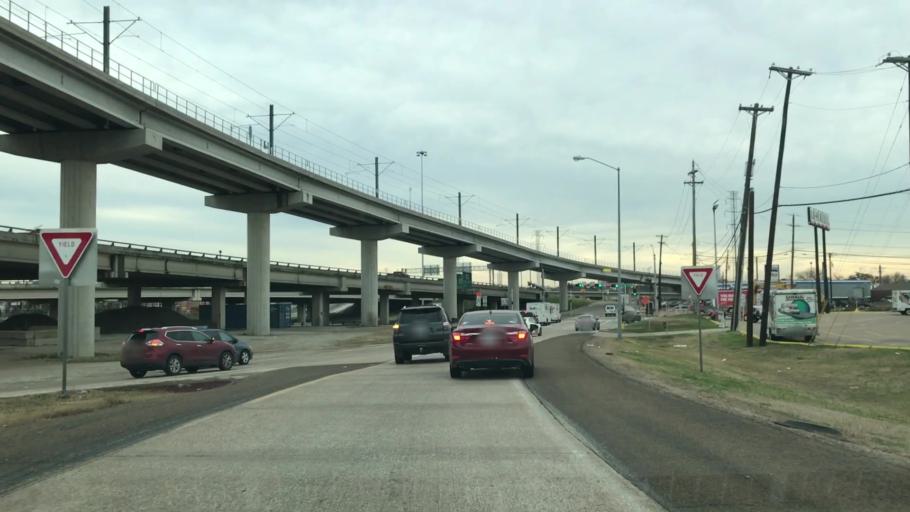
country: US
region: Texas
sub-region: Dallas County
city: Farmers Branch
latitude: 32.8572
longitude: -96.8821
